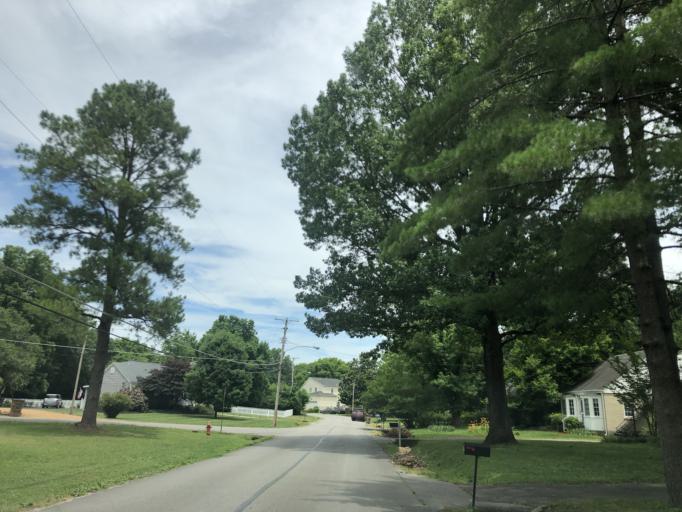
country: US
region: Tennessee
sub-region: Davidson County
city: Oak Hill
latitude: 36.1090
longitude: -86.7848
